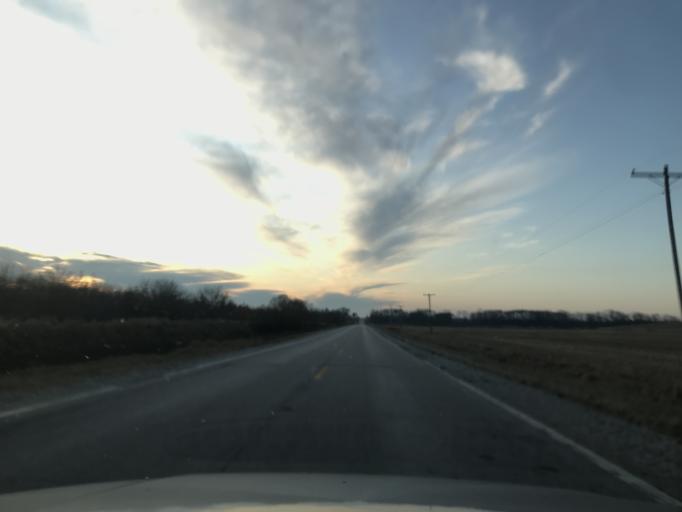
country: US
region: Illinois
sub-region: Henderson County
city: Oquawka
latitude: 41.0191
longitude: -90.8154
